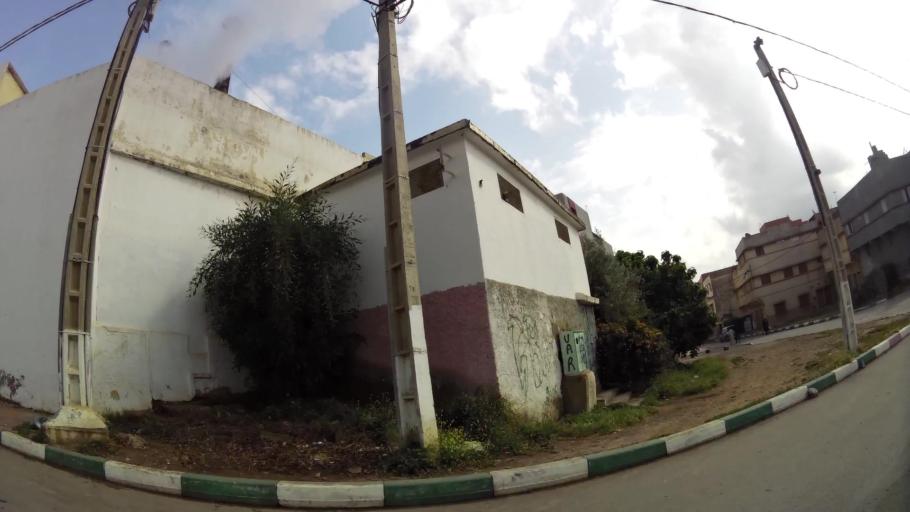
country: MA
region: Rabat-Sale-Zemmour-Zaer
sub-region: Khemisset
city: Tiflet
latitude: 33.8939
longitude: -6.3169
